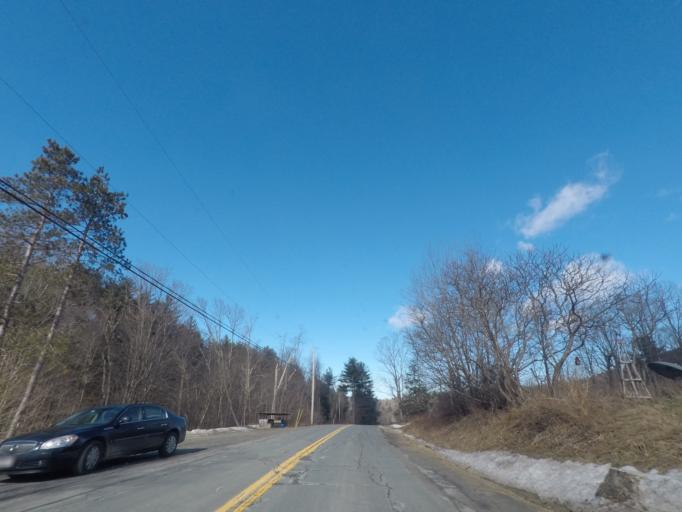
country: US
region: Massachusetts
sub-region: Berkshire County
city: Williamstown
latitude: 42.7367
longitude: -73.3367
